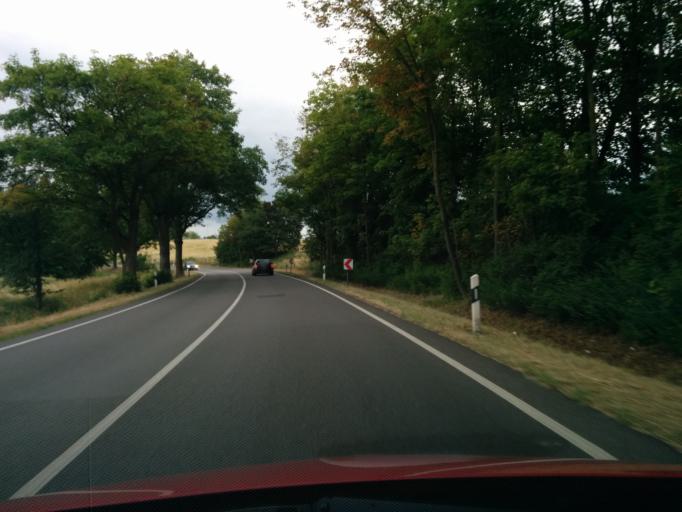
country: DE
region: Thuringia
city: Gebesee
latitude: 51.1214
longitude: 10.9266
